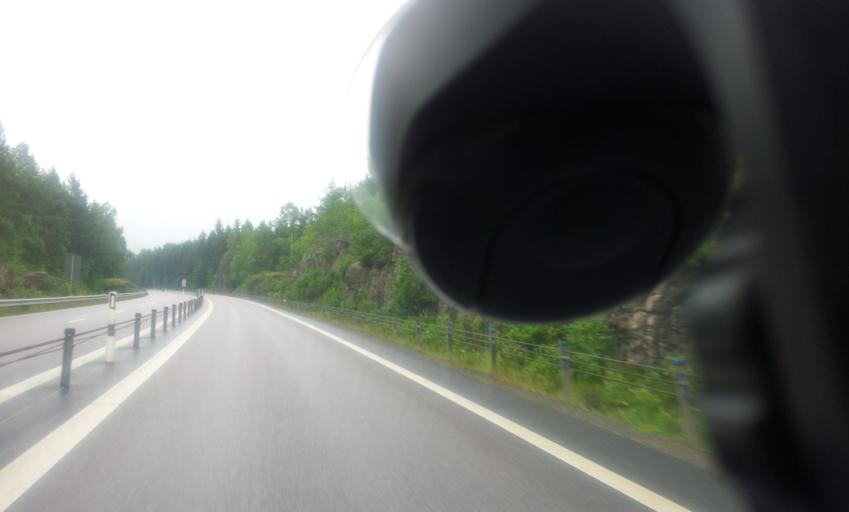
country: SE
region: Kalmar
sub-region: Vasterviks Kommun
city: Forserum
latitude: 58.0333
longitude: 16.5152
